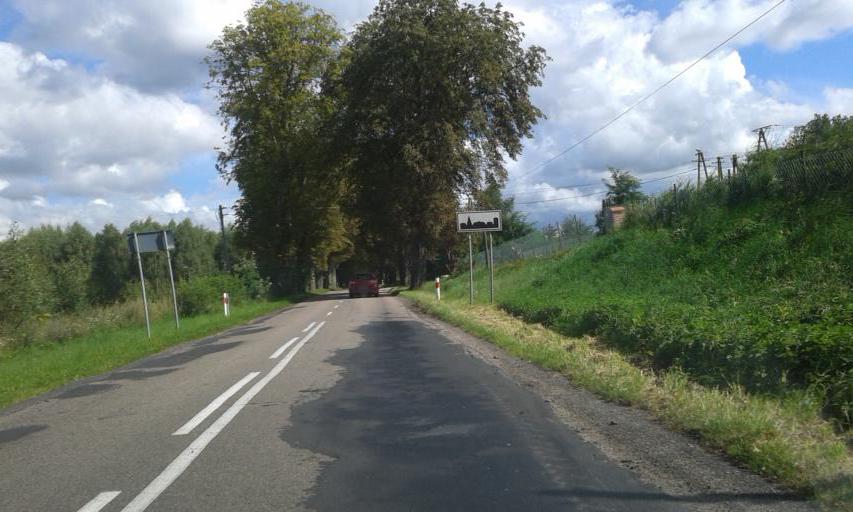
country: PL
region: West Pomeranian Voivodeship
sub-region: Powiat koszalinski
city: Polanow
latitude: 54.2067
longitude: 16.6995
